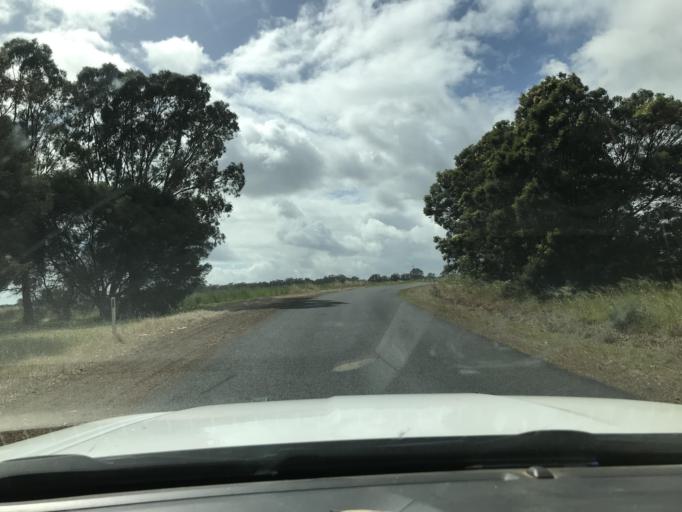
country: AU
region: South Australia
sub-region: Wattle Range
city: Penola
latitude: -37.1460
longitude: 141.3937
